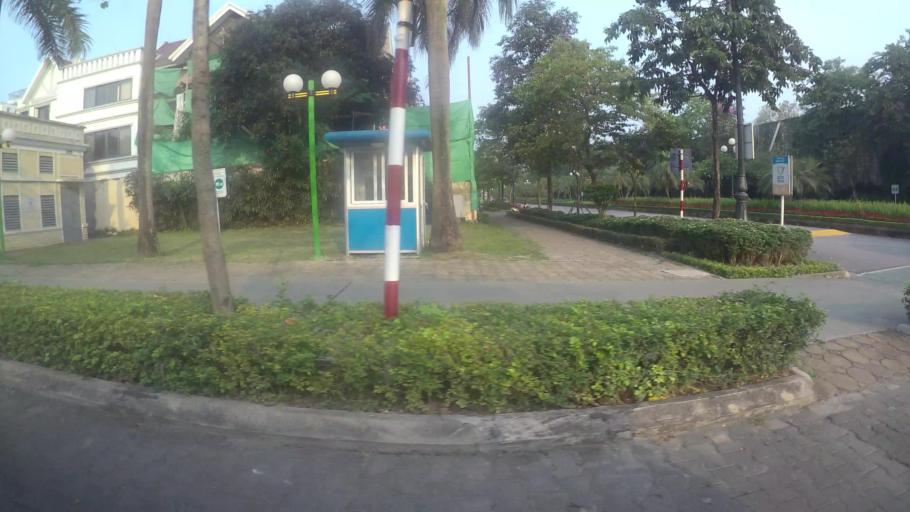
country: VN
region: Ha Noi
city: Tay Ho
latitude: 21.0774
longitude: 105.7948
